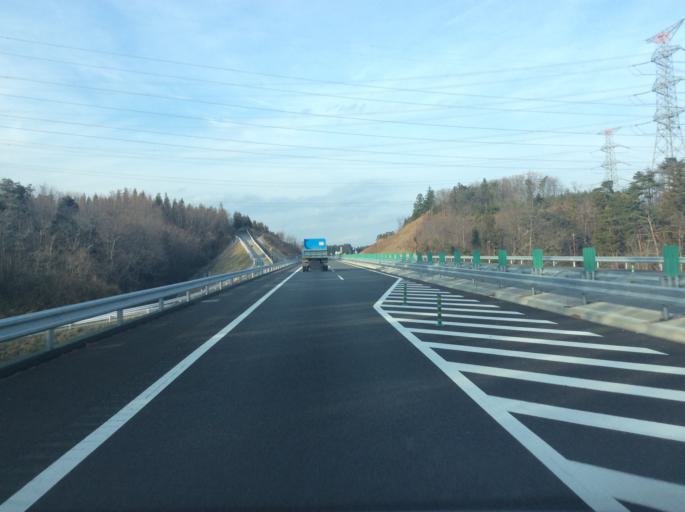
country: JP
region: Fukushima
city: Namie
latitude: 37.5264
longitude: 140.9422
